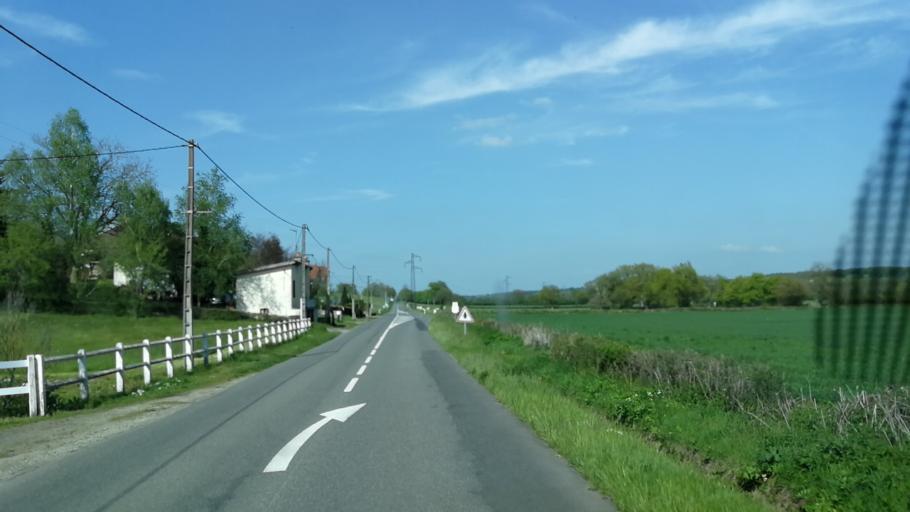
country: FR
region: Auvergne
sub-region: Departement de l'Allier
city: Lapalisse
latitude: 46.3849
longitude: 3.5851
